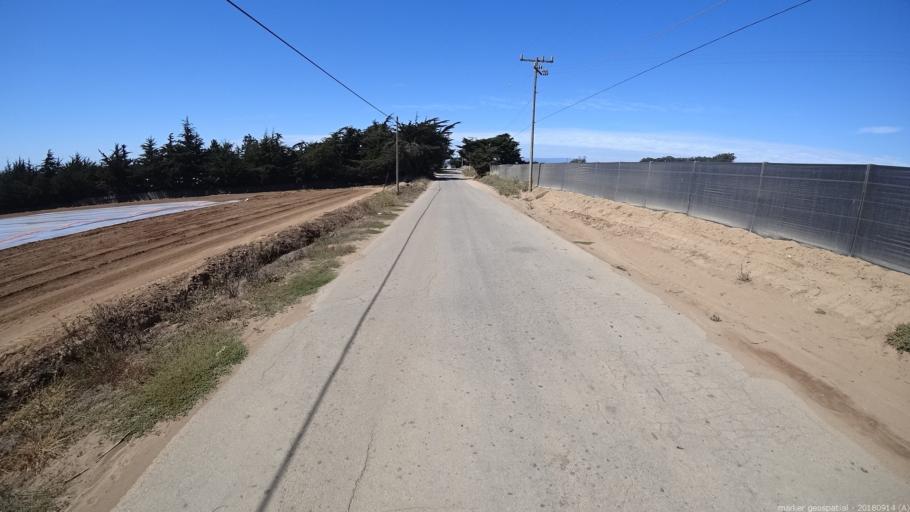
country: US
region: California
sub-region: Monterey County
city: Las Lomas
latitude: 36.8541
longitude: -121.7898
